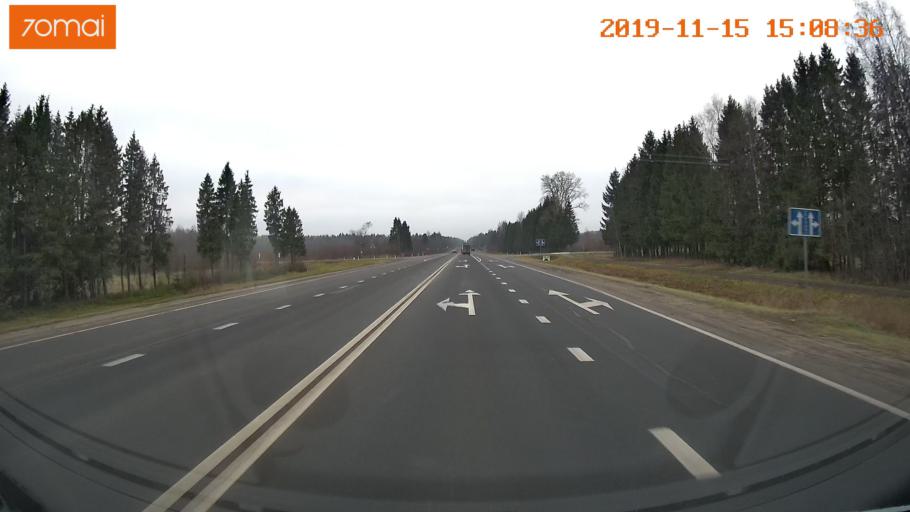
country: RU
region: Jaroslavl
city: Prechistoye
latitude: 58.3689
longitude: 40.2749
